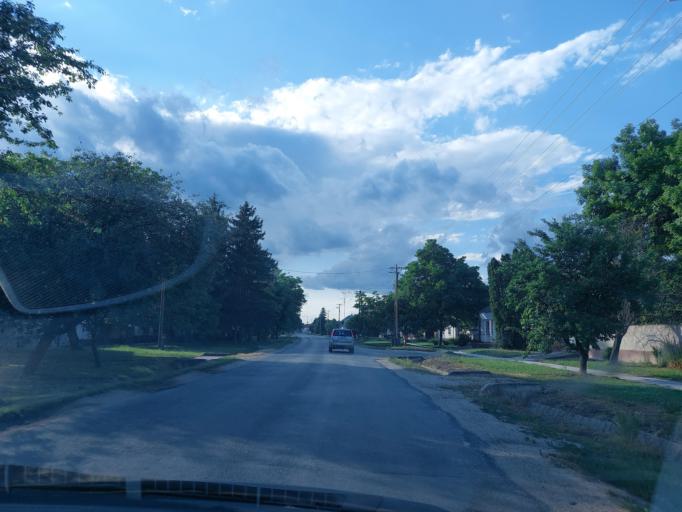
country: HU
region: Veszprem
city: Devecser
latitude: 47.1713
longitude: 17.3590
